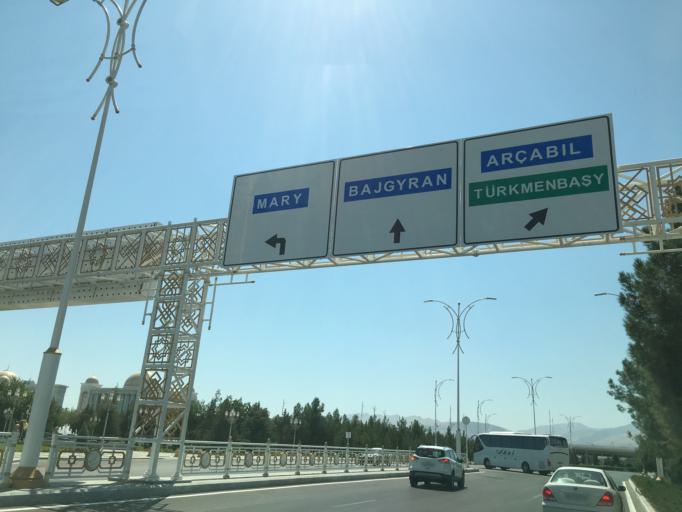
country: TM
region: Ahal
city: Ashgabat
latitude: 37.8818
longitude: 58.3772
